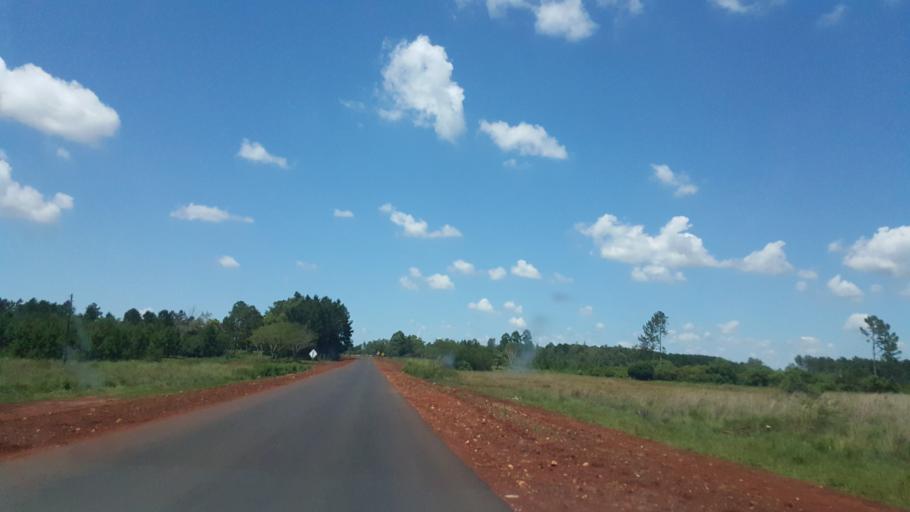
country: AR
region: Corrientes
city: Santo Tome
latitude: -28.5016
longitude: -56.0542
